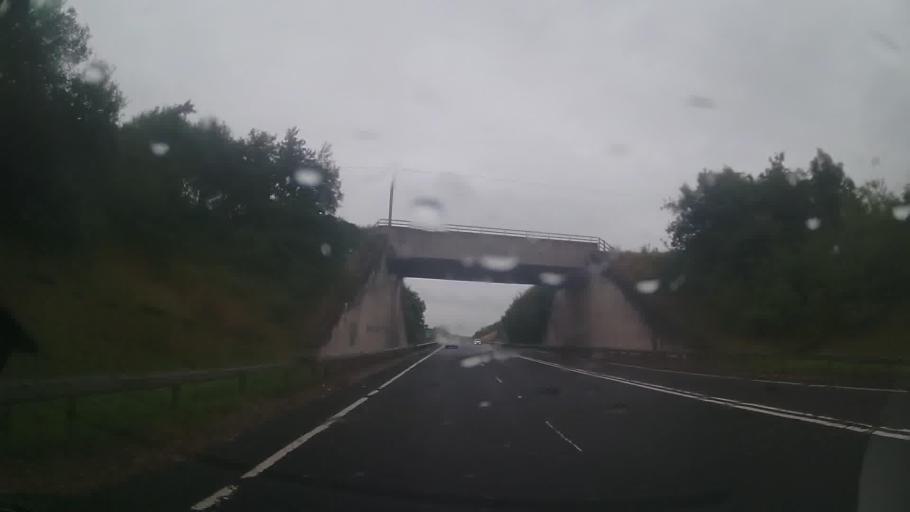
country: GB
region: Scotland
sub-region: North Ayrshire
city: Ardrossan
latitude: 55.6562
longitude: -4.8227
